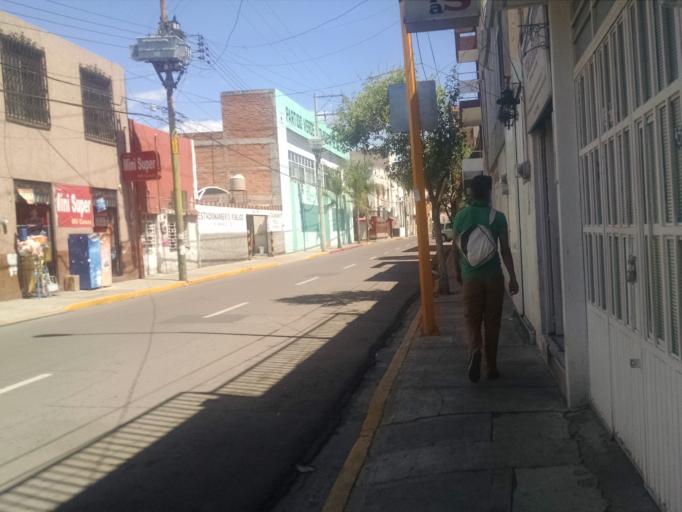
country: MX
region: Aguascalientes
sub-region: Aguascalientes
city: Aguascalientes
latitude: 21.8787
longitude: -102.3019
